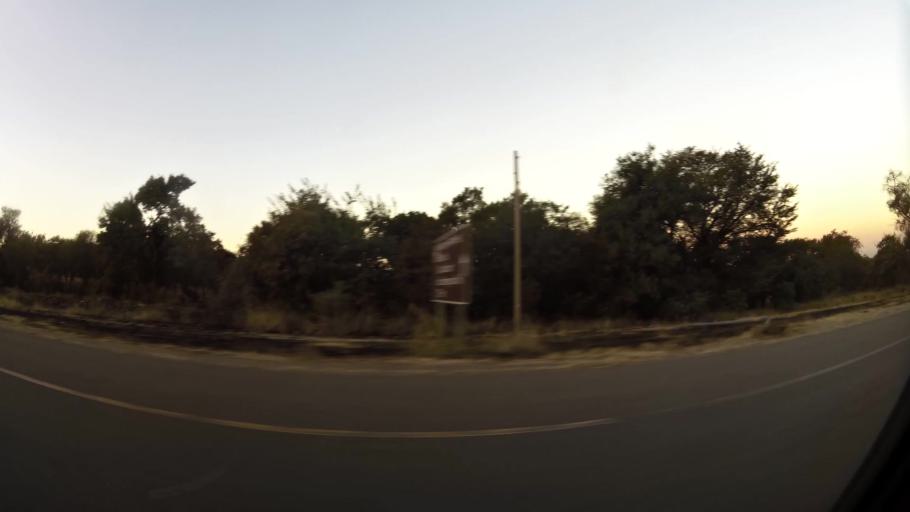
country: ZA
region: North-West
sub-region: Bojanala Platinum District Municipality
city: Rustenburg
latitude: -25.6360
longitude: 27.1950
